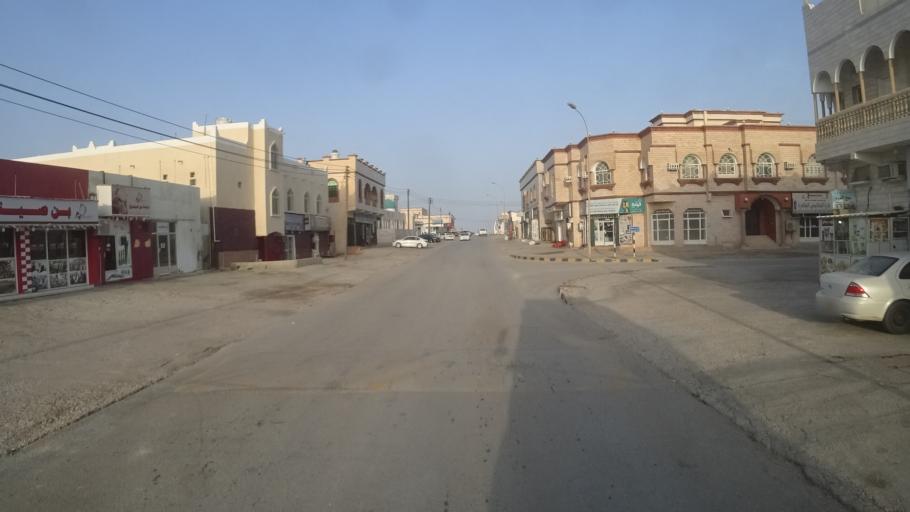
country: OM
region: Zufar
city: Salalah
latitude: 16.9827
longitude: 54.6908
